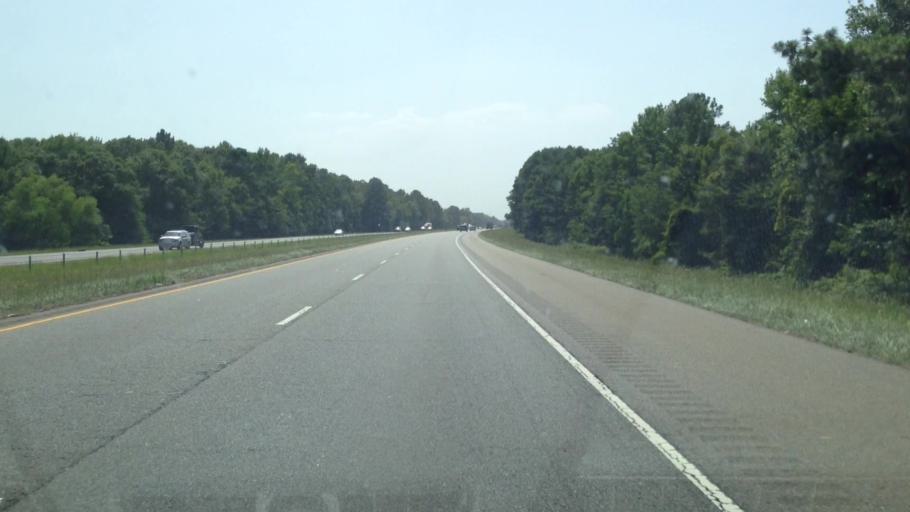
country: US
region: Louisiana
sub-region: Bossier Parish
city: Haughton
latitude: 32.5775
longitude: -93.4480
